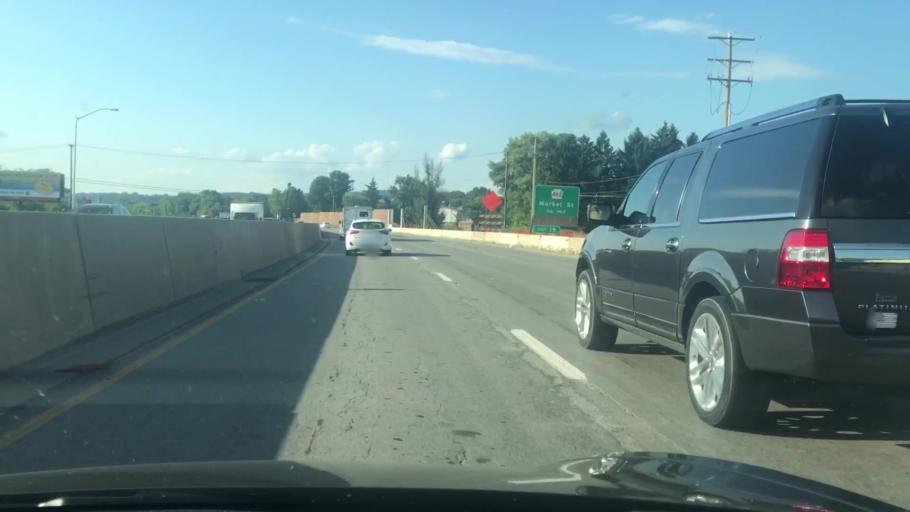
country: US
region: Pennsylvania
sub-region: York County
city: East York
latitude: 39.9609
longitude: -76.6850
